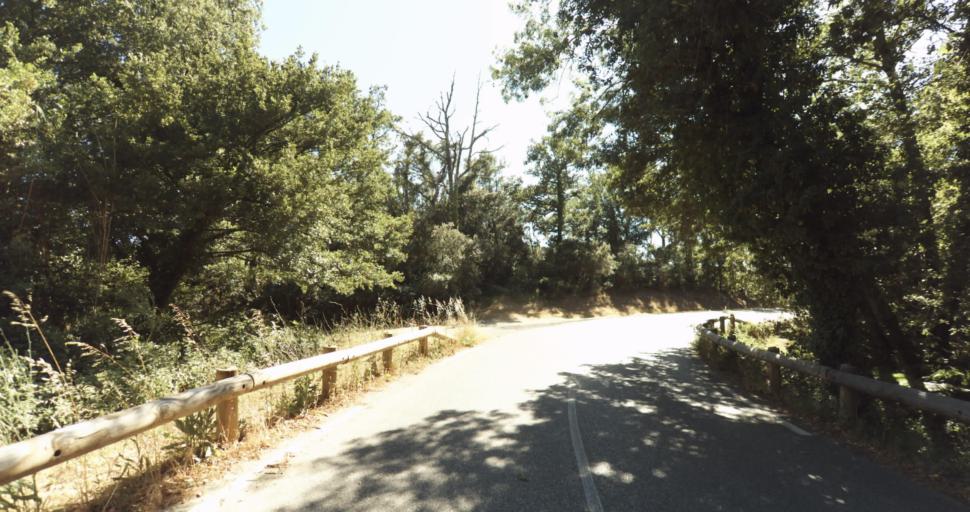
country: FR
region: Provence-Alpes-Cote d'Azur
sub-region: Departement du Var
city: Gassin
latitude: 43.2519
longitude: 6.5984
